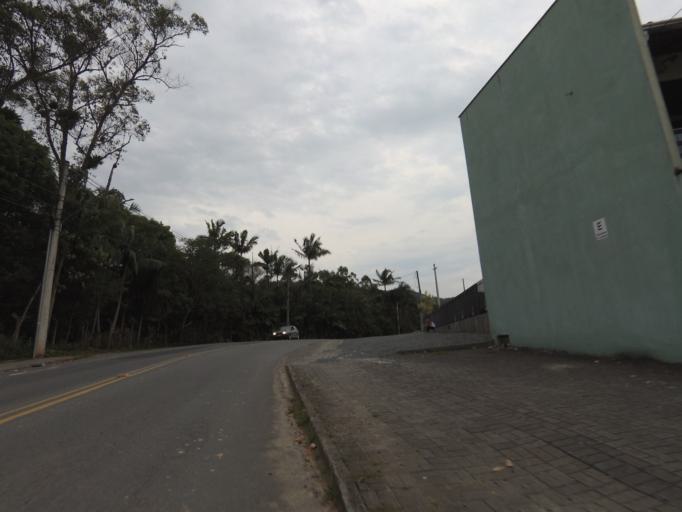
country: BR
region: Santa Catarina
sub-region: Blumenau
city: Blumenau
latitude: -26.8659
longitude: -49.0505
